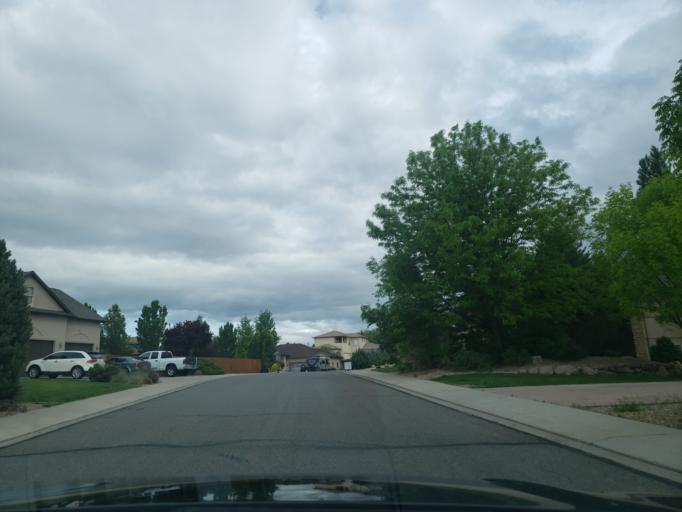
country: US
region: Colorado
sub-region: Mesa County
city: Redlands
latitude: 39.1053
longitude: -108.6683
